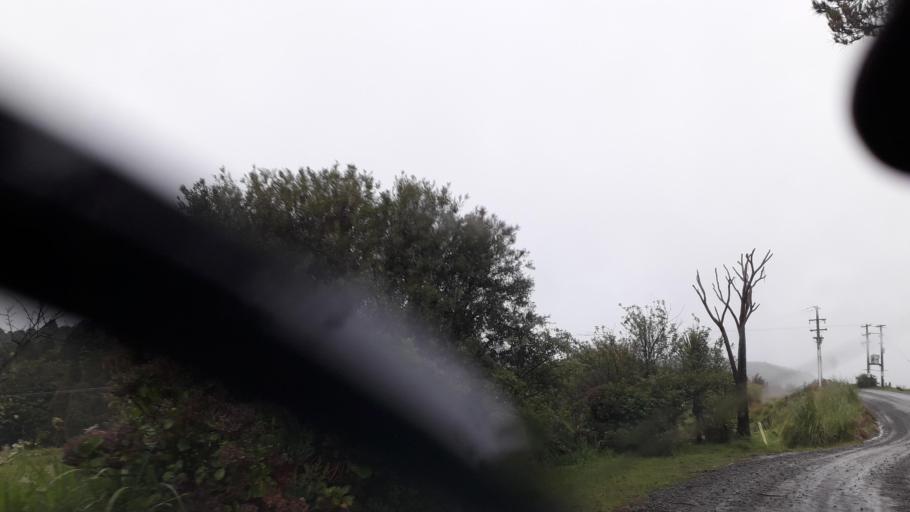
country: NZ
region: Northland
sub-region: Far North District
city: Kerikeri
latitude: -35.1220
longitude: 173.7474
